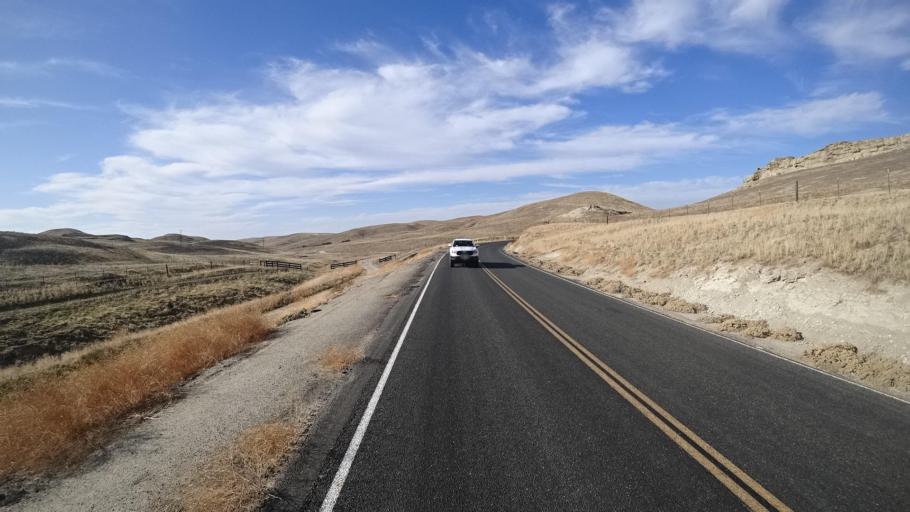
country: US
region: California
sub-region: Kern County
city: Oildale
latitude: 35.6093
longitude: -118.9227
